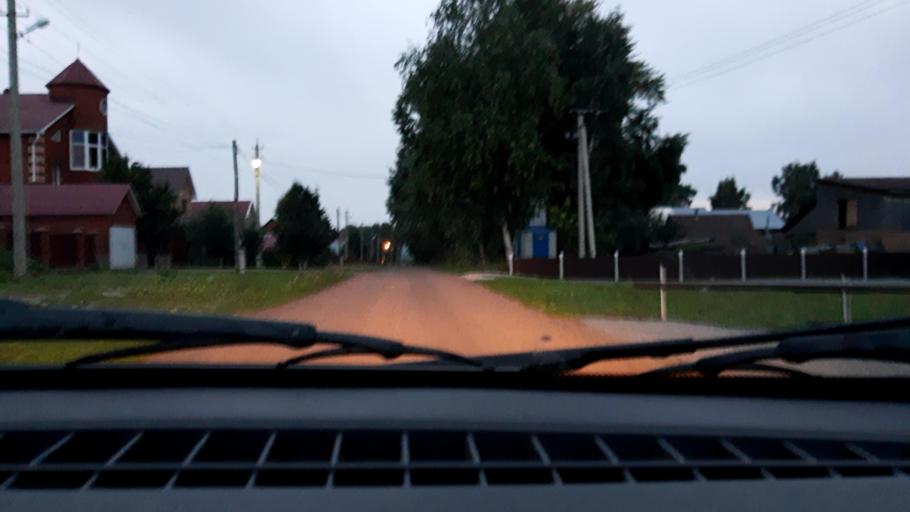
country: RU
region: Bashkortostan
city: Mikhaylovka
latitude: 54.8606
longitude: 55.8031
